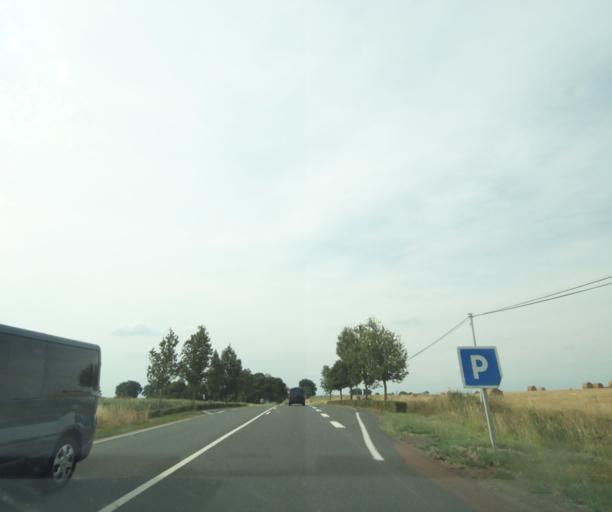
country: FR
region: Pays de la Loire
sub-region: Departement de la Sarthe
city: Luceau
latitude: 47.7244
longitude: 0.3979
